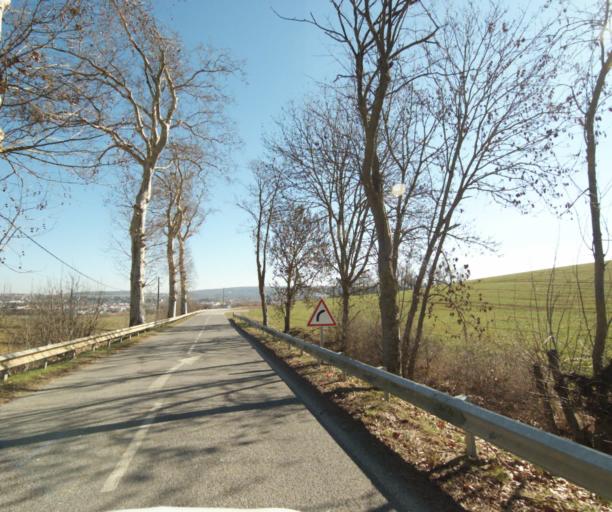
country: FR
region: Lorraine
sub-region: Departement de Meurthe-et-Moselle
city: Essey-les-Nancy
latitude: 48.7152
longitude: 6.2391
